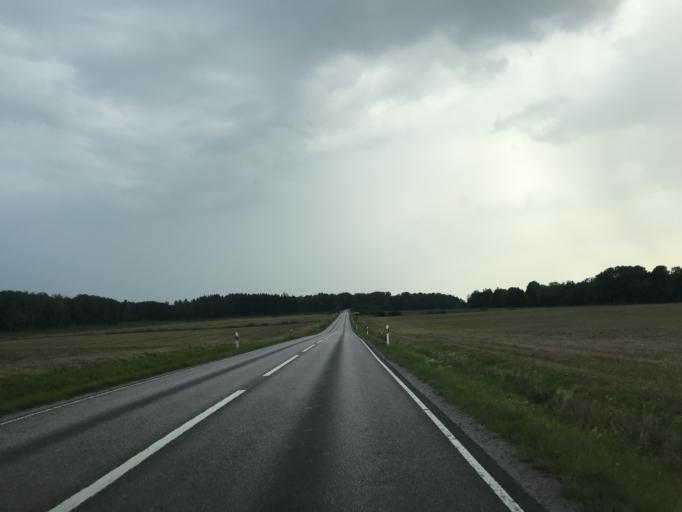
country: SE
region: Stockholm
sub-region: Norrtalje Kommun
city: Norrtalje
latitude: 59.8279
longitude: 18.6551
